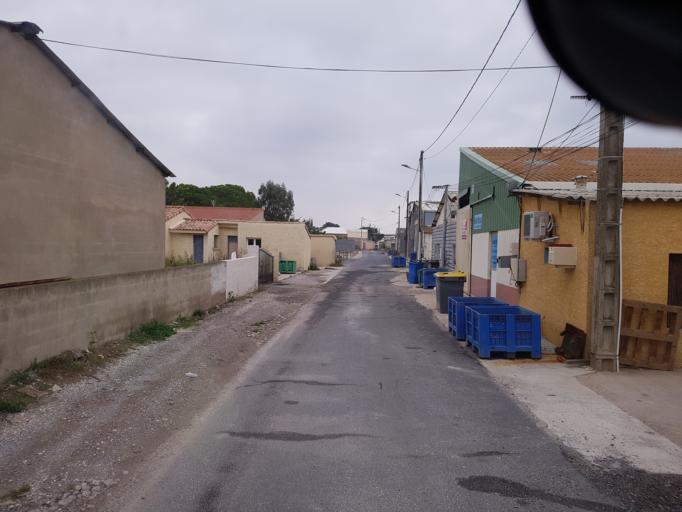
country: FR
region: Languedoc-Roussillon
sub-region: Departement de l'Herault
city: Marseillan
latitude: 43.3638
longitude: 3.5370
